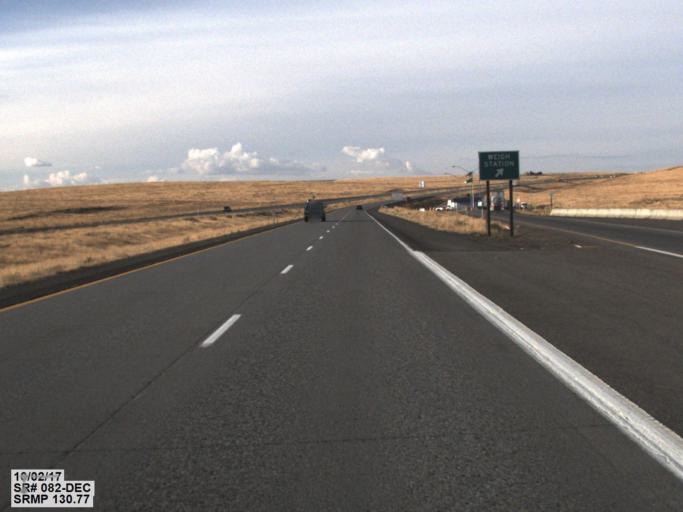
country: US
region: Oregon
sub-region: Umatilla County
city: Umatilla
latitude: 45.9568
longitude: -119.3404
